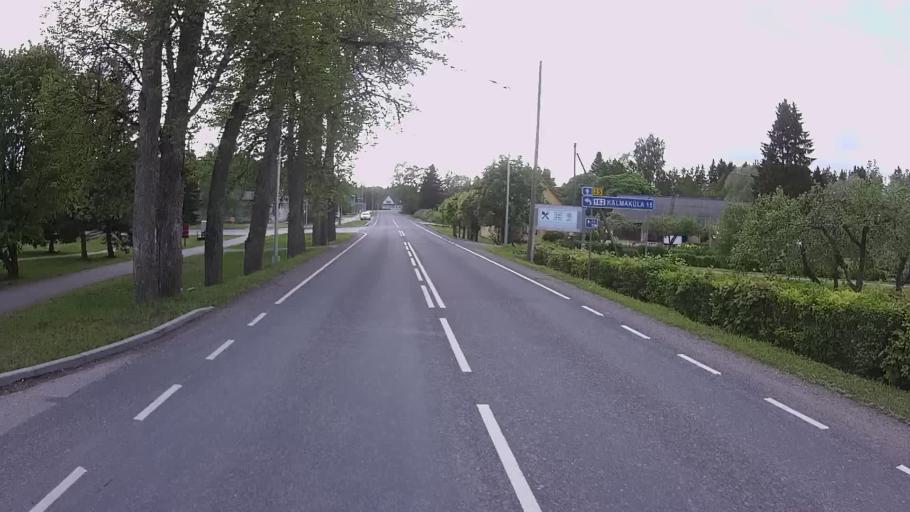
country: EE
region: Jogevamaa
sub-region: Mustvee linn
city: Mustvee
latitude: 58.9852
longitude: 26.8636
